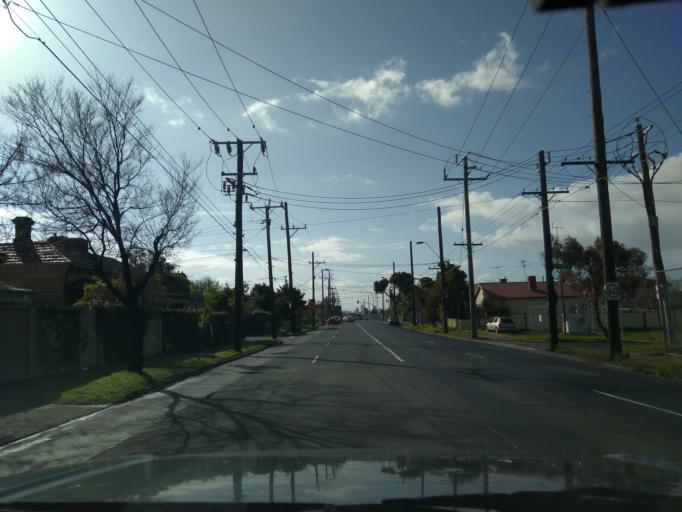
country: AU
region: Victoria
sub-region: Maribyrnong
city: Yarraville
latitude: -37.8216
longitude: 144.8938
